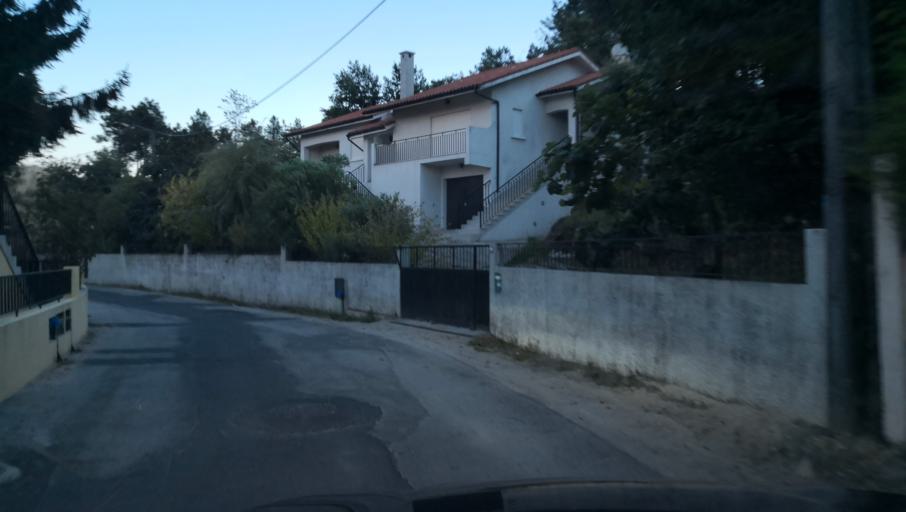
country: PT
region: Vila Real
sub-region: Santa Marta de Penaguiao
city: Santa Marta de Penaguiao
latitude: 41.2682
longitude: -7.8089
